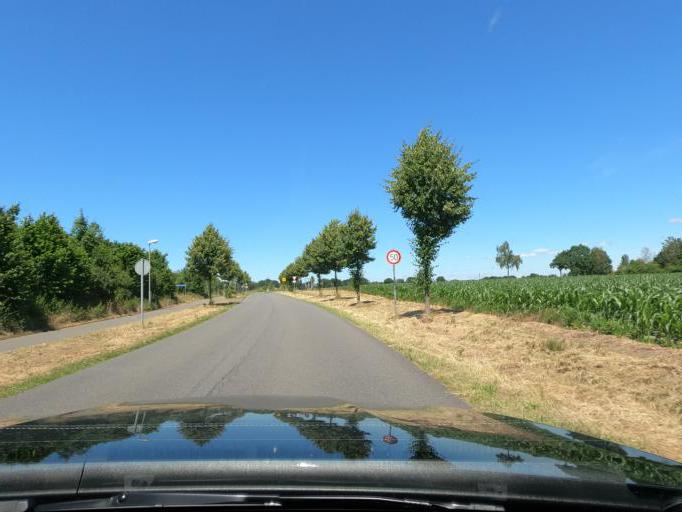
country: DE
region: Lower Saxony
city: Lachendorf
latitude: 52.6183
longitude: 10.2579
